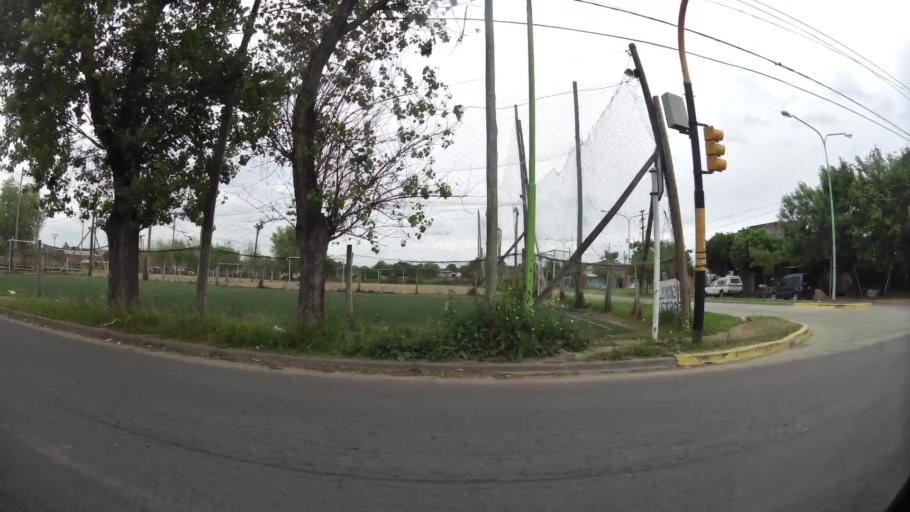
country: AR
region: Buenos Aires
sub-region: Partido de Campana
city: Campana
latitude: -34.1826
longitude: -58.9431
